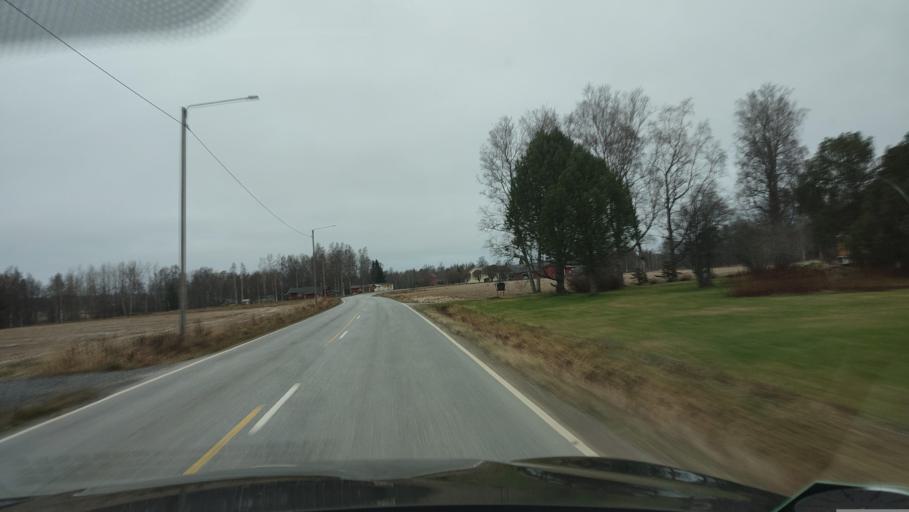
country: FI
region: Southern Ostrobothnia
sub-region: Suupohja
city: Karijoki
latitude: 62.2736
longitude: 21.7077
